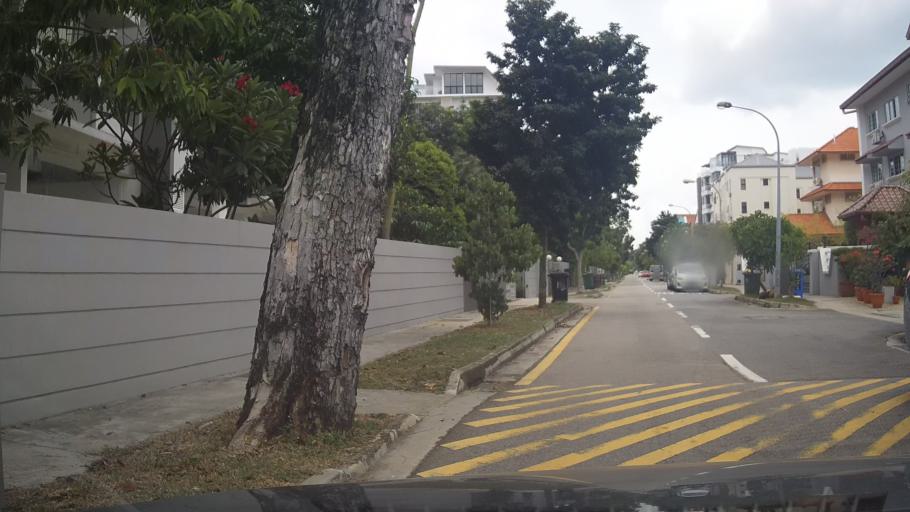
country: SG
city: Singapore
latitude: 1.3103
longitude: 103.9093
